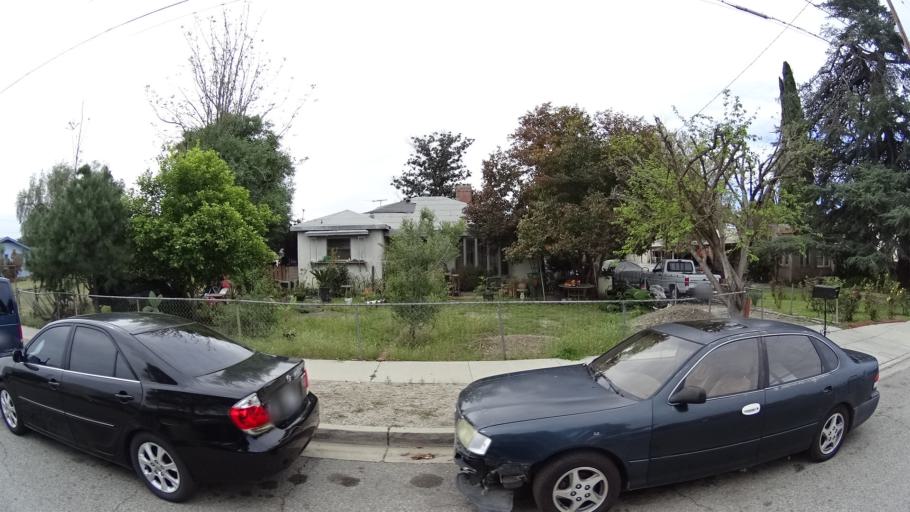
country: US
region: California
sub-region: Los Angeles County
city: Baldwin Park
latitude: 34.0785
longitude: -117.9724
